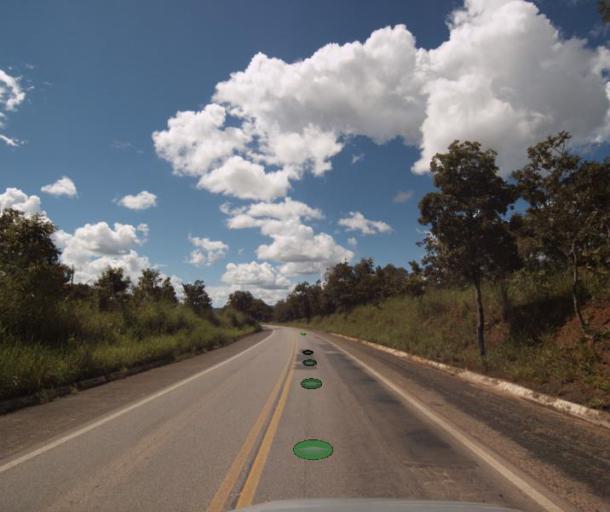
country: BR
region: Goias
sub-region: Porangatu
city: Porangatu
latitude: -13.7257
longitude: -49.0216
